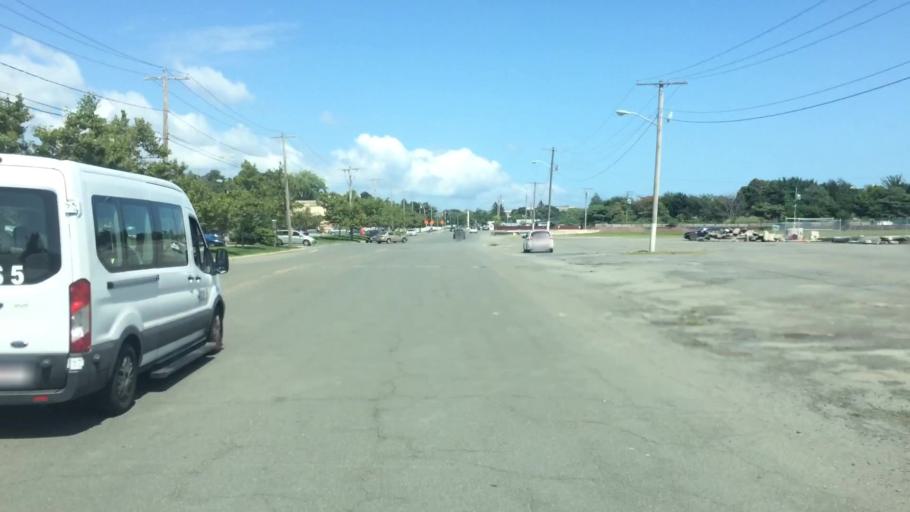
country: US
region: Massachusetts
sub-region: Suffolk County
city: Revere
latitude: 42.3972
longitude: -71.0003
